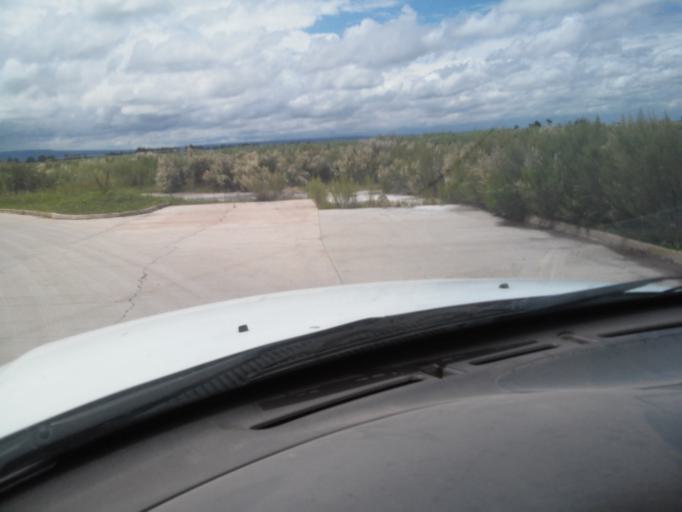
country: MX
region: Durango
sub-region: Durango
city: Jose Refugio Salcido
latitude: 24.0171
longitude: -104.5471
